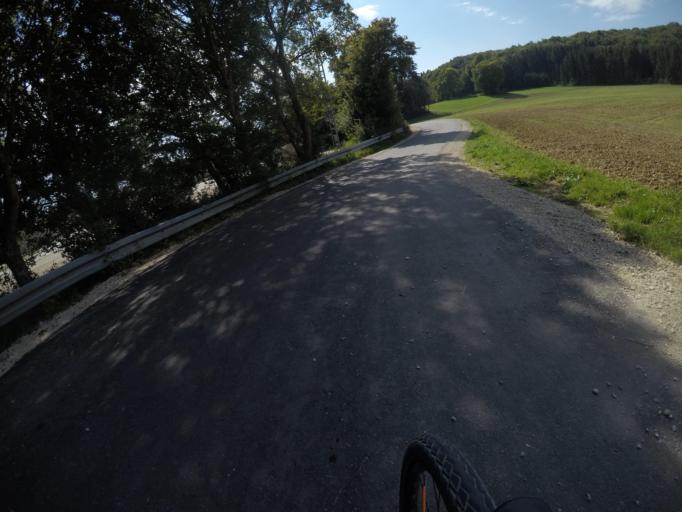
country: DE
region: Baden-Wuerttemberg
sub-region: Tuebingen Region
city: Munsingen
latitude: 48.3795
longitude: 9.5142
